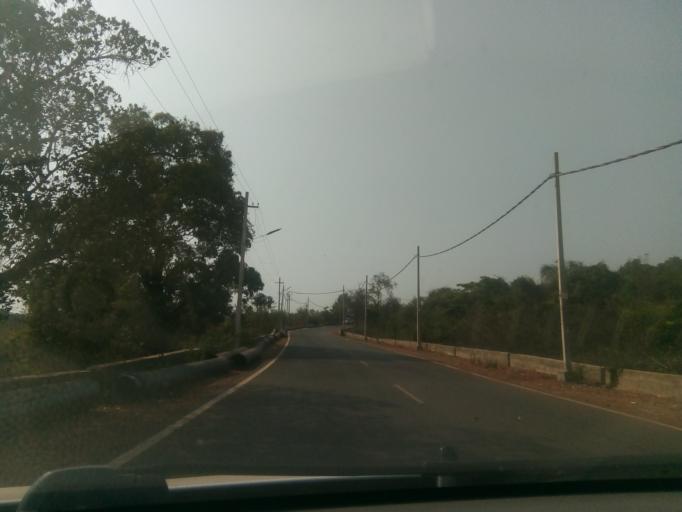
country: IN
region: Goa
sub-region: North Goa
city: Pernem
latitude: 15.7191
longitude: 73.8536
